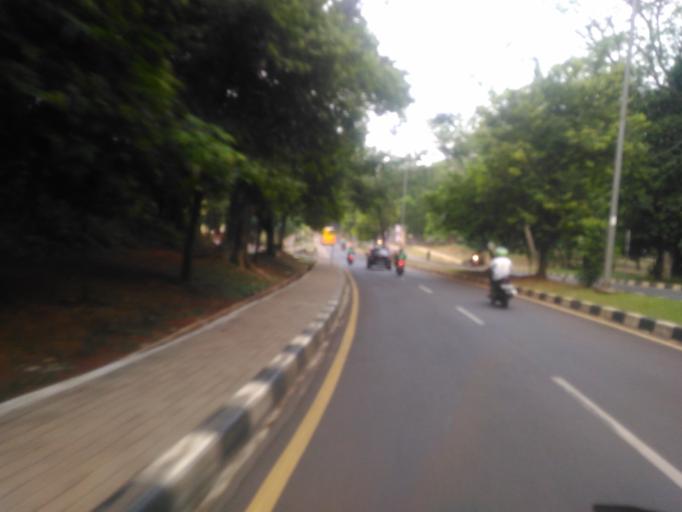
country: ID
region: West Java
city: Depok
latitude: -6.3668
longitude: 106.8227
